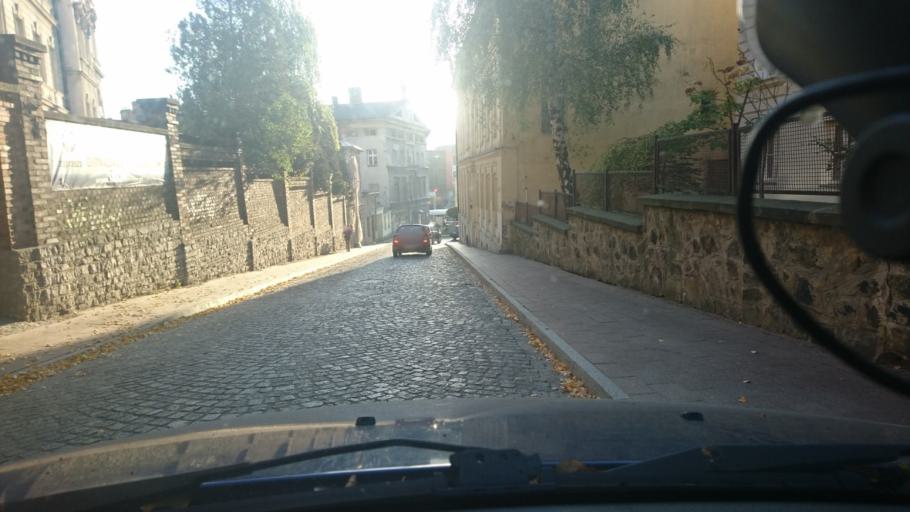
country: PL
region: Silesian Voivodeship
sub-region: Bielsko-Biala
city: Bielsko-Biala
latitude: 49.8197
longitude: 19.0425
